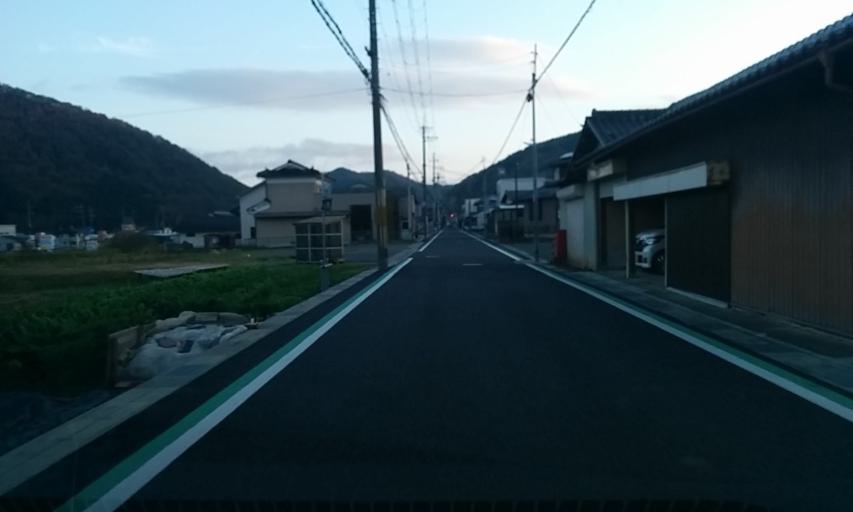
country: JP
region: Kyoto
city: Ayabe
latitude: 35.1594
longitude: 135.4249
